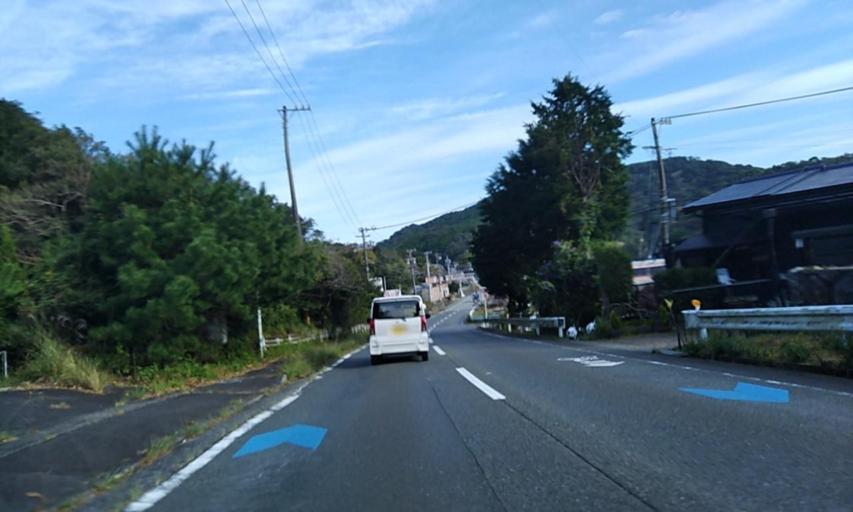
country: JP
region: Mie
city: Ise
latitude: 34.3447
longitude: 136.7239
